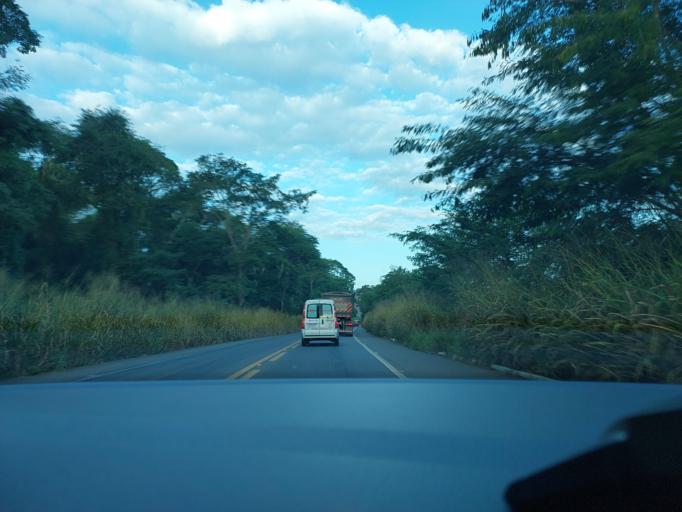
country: BR
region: Minas Gerais
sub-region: Muriae
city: Muriae
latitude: -21.1464
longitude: -42.1669
